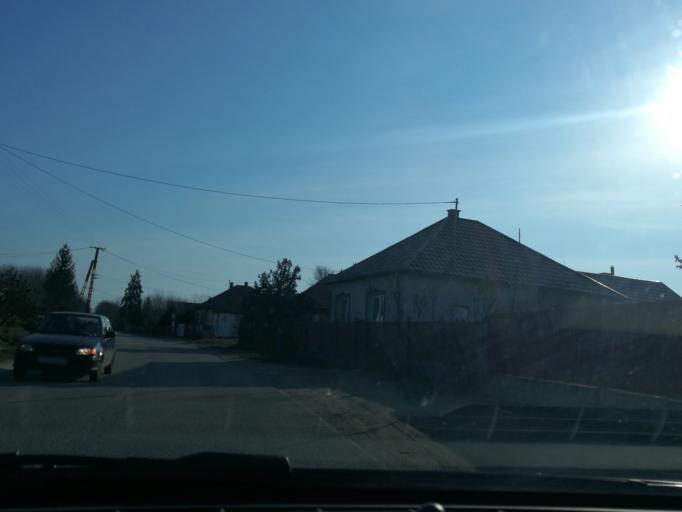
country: HU
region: Szabolcs-Szatmar-Bereg
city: Nyirbogdany
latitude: 48.0565
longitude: 21.9441
